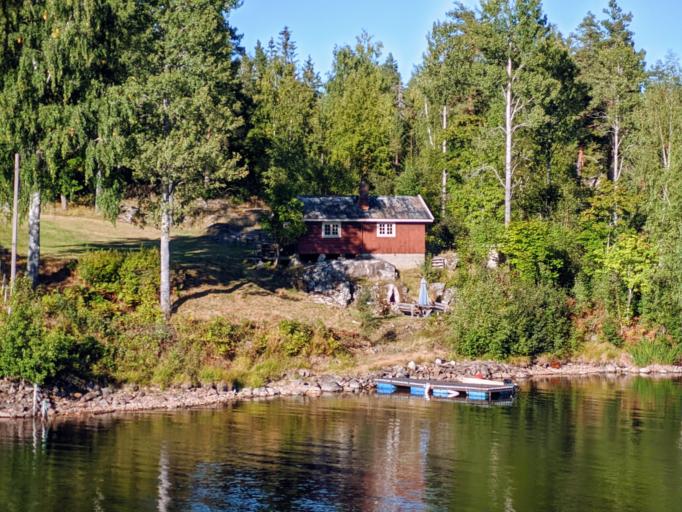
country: NO
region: Akershus
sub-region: Eidsvoll
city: Raholt
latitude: 60.2854
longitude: 11.1261
